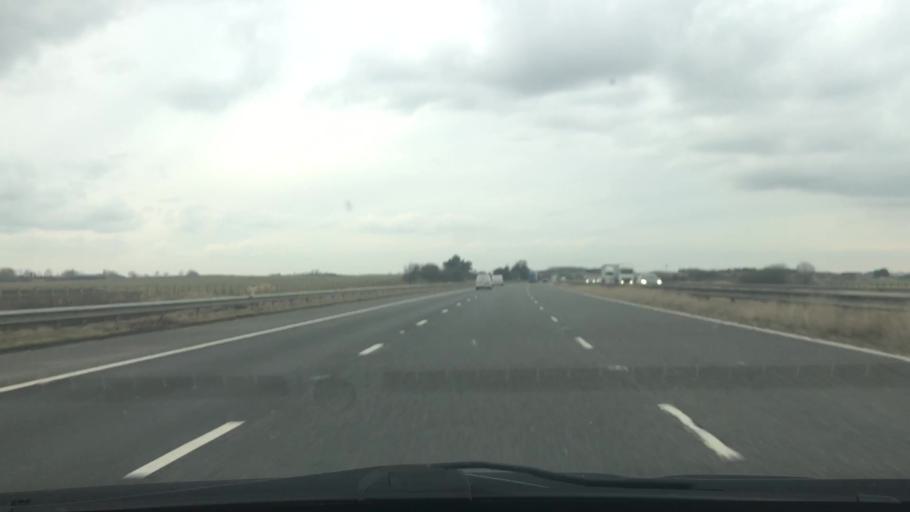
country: GB
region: England
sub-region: Doncaster
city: Hatfield
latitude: 53.5829
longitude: -0.9504
